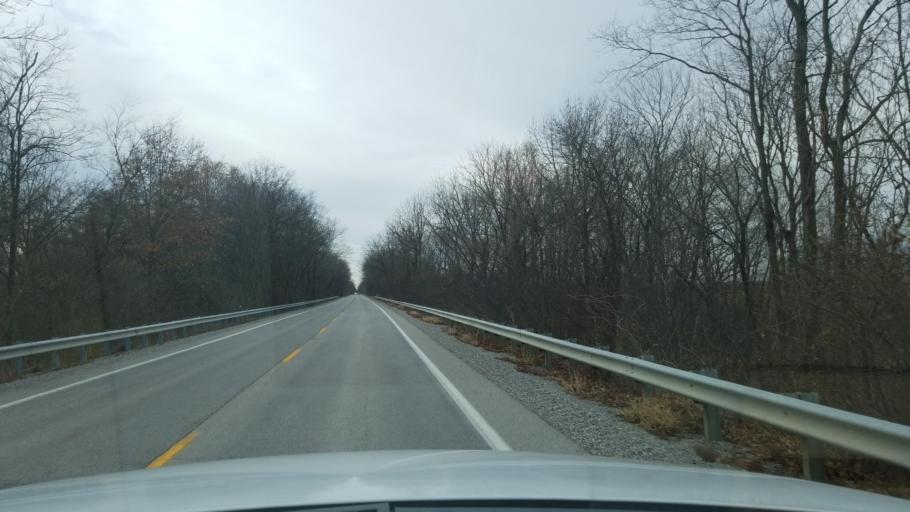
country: US
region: Illinois
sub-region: White County
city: Carmi
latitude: 37.9344
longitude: -88.0836
